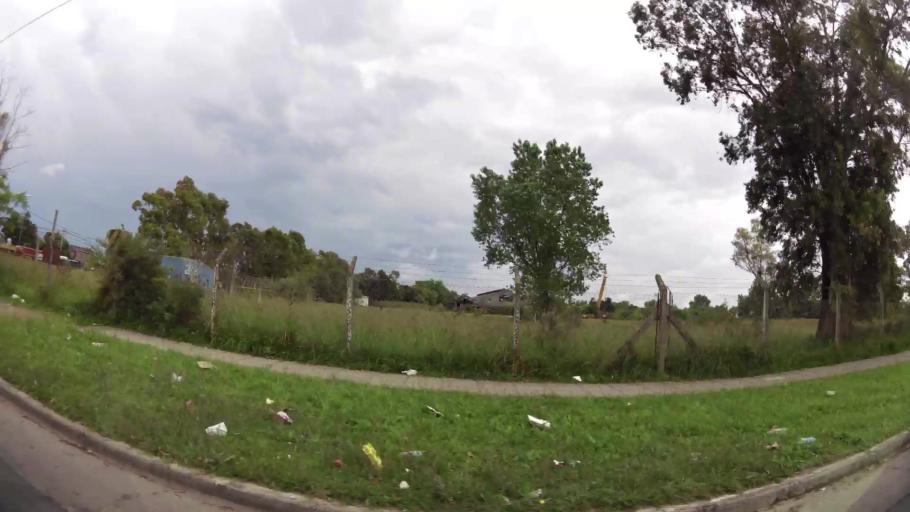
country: AR
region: Buenos Aires
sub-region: Partido de Quilmes
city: Quilmes
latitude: -34.7475
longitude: -58.2913
